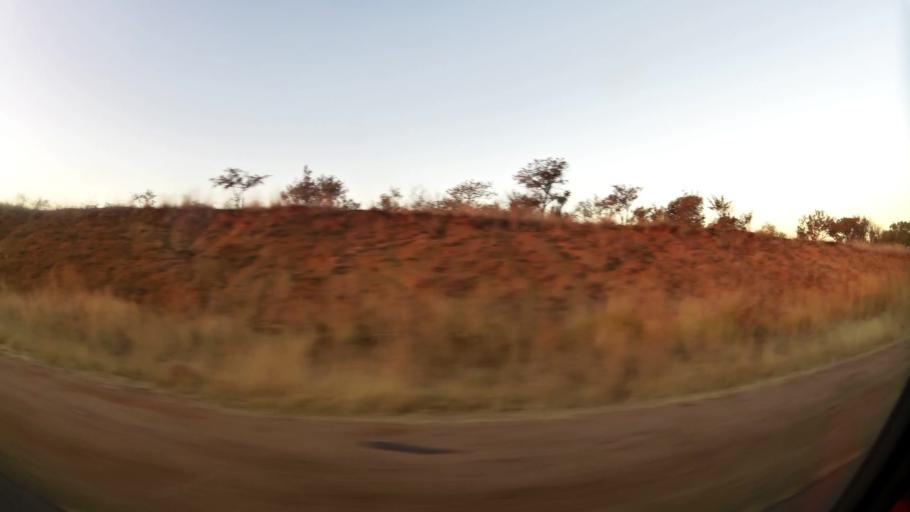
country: ZA
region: North-West
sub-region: Bojanala Platinum District Municipality
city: Rustenburg
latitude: -25.6202
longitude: 27.1818
